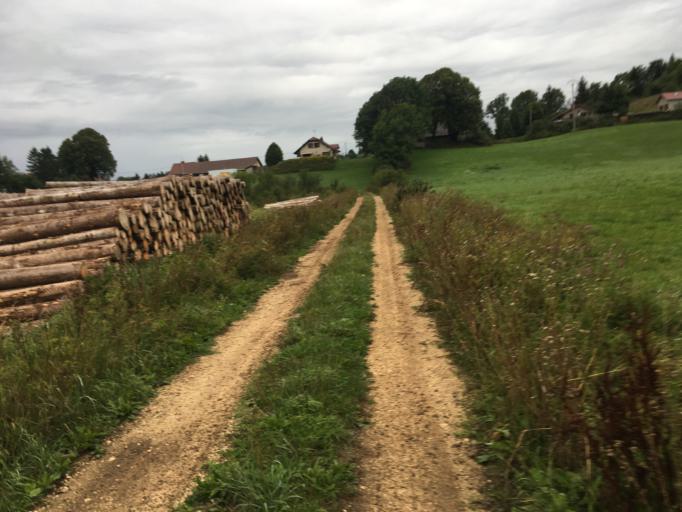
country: FR
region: Franche-Comte
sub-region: Departement du Jura
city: Morbier
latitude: 46.6128
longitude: 5.9749
